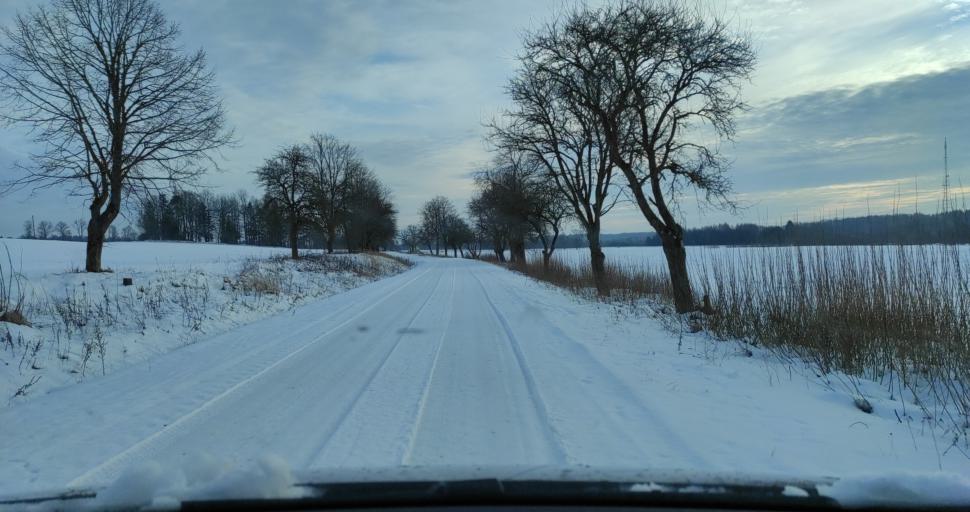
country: LV
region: Kuldigas Rajons
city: Kuldiga
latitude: 56.9515
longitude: 22.0178
